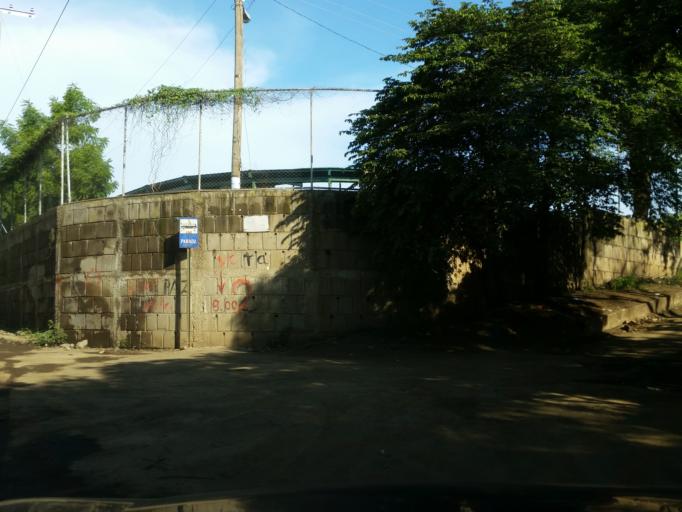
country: NI
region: Managua
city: Managua
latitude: 12.0968
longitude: -86.2076
